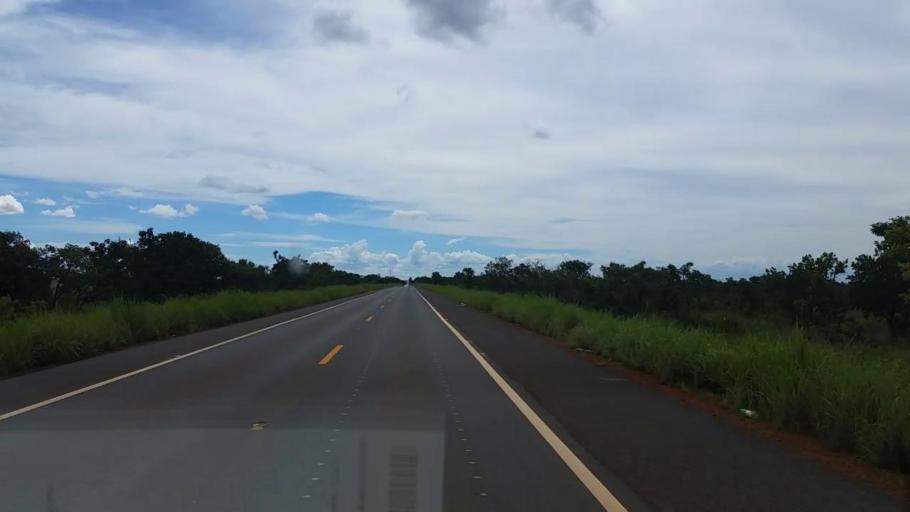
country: BR
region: Goias
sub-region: Luziania
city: Luziania
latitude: -16.2086
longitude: -47.4227
